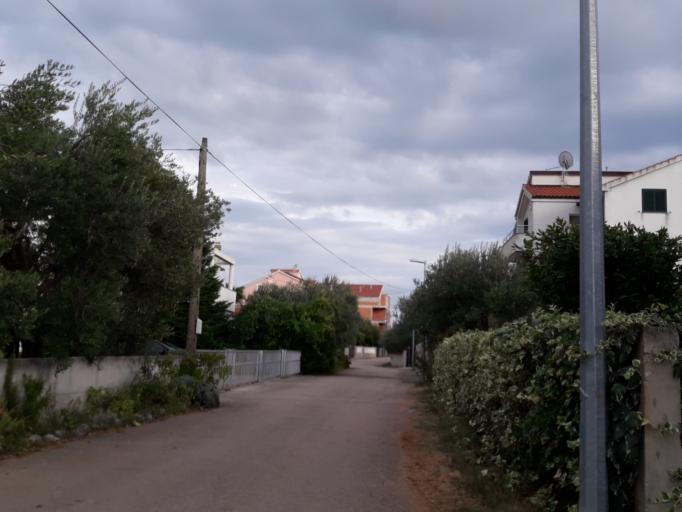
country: HR
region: Sibensko-Kniniska
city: Vodice
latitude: 43.7479
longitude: 15.7980
